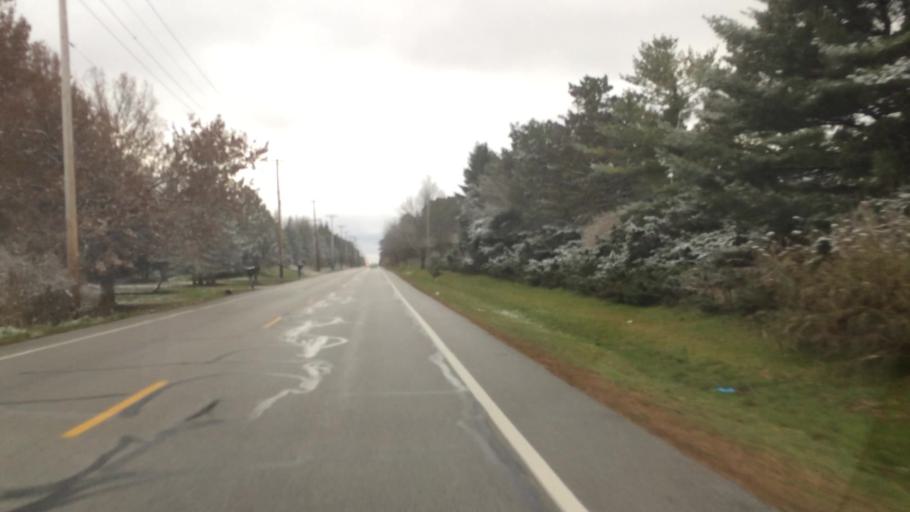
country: US
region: Ohio
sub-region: Summit County
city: Hudson
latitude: 41.2375
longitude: -81.4111
